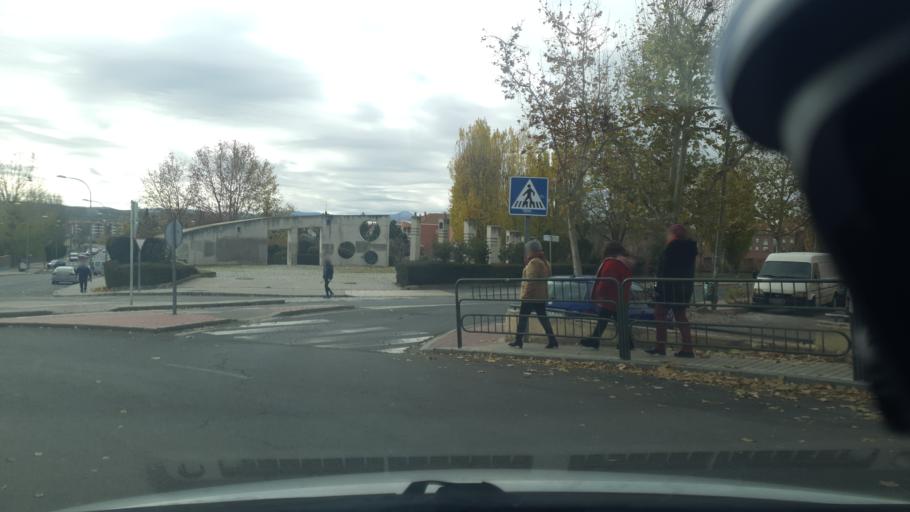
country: ES
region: Castille and Leon
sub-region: Provincia de Avila
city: Avila
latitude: 40.6484
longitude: -4.6876
